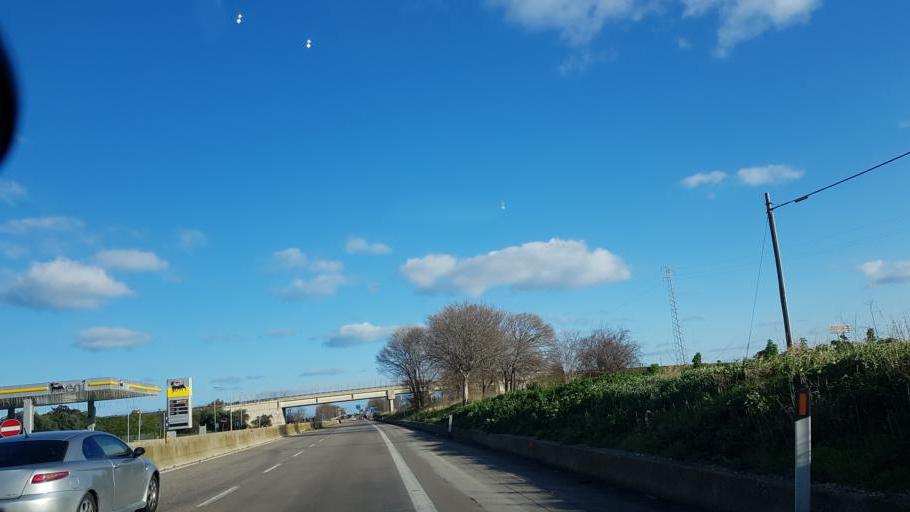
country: IT
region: Apulia
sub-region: Provincia di Brindisi
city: Brindisi
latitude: 40.6188
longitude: 17.9427
